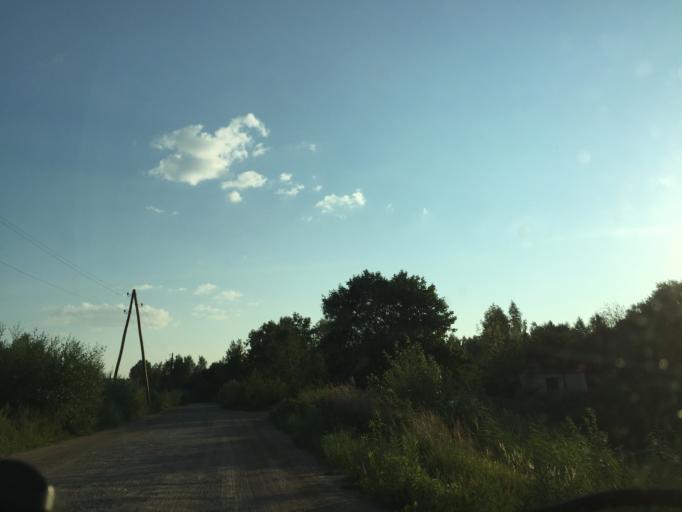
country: LV
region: Riga
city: Bergi
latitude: 56.9756
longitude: 24.3482
